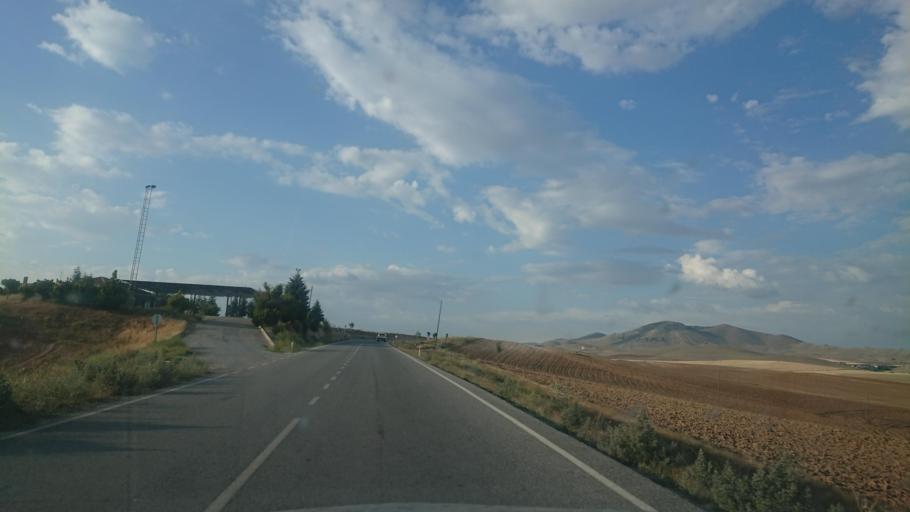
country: TR
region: Aksaray
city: Aksaray
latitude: 38.5042
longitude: 34.0803
